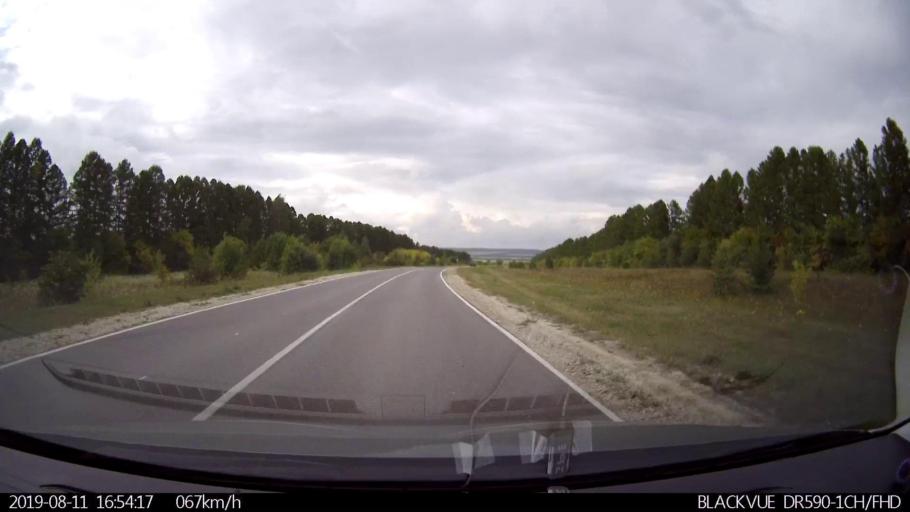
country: RU
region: Ulyanovsk
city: Mayna
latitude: 54.2711
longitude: 47.6664
